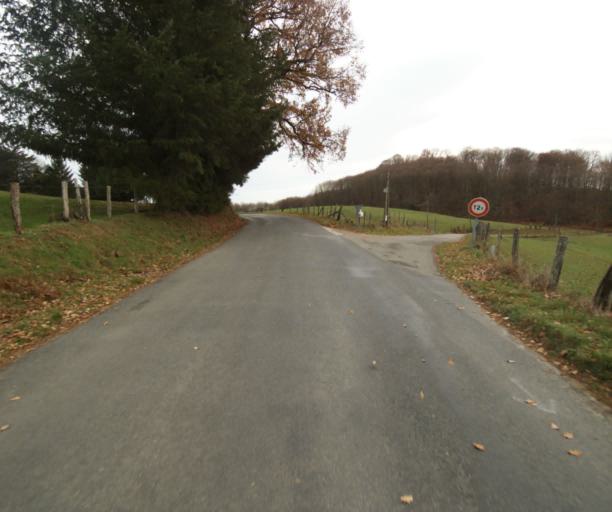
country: FR
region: Limousin
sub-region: Departement de la Correze
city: Chameyrat
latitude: 45.2585
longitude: 1.6779
